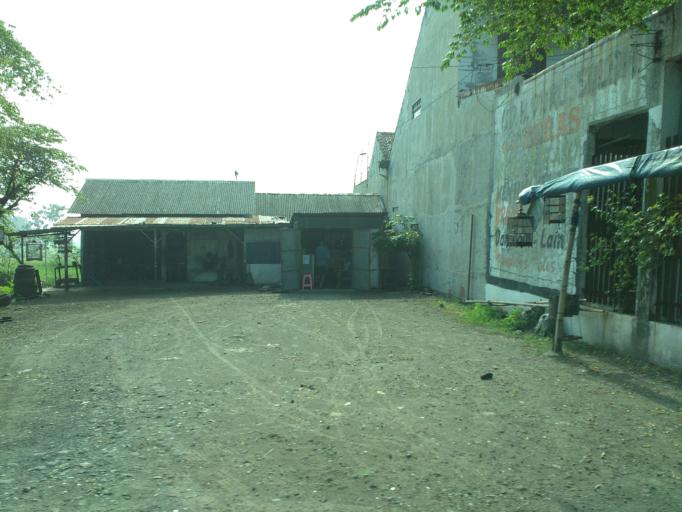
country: ID
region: Central Java
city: Gatak
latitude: -7.6098
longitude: 110.7016
